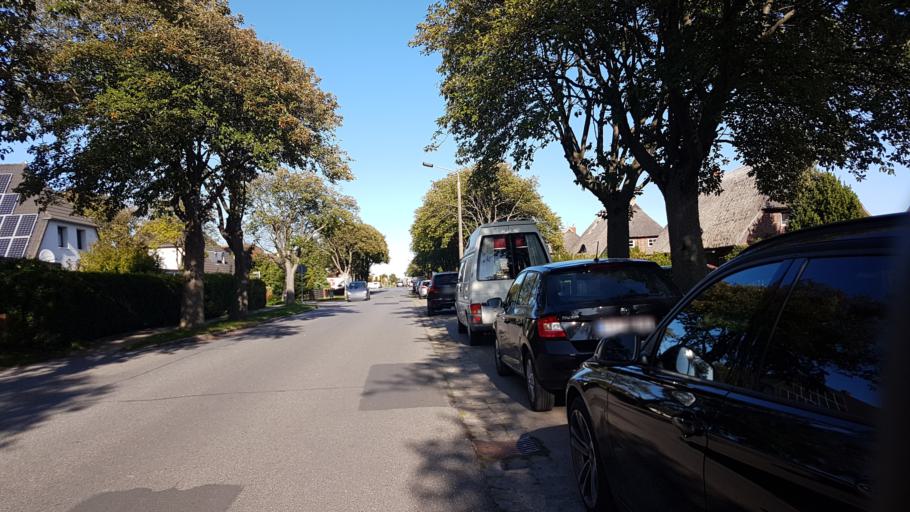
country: DE
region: Mecklenburg-Vorpommern
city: Dranske
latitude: 54.6294
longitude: 13.2319
